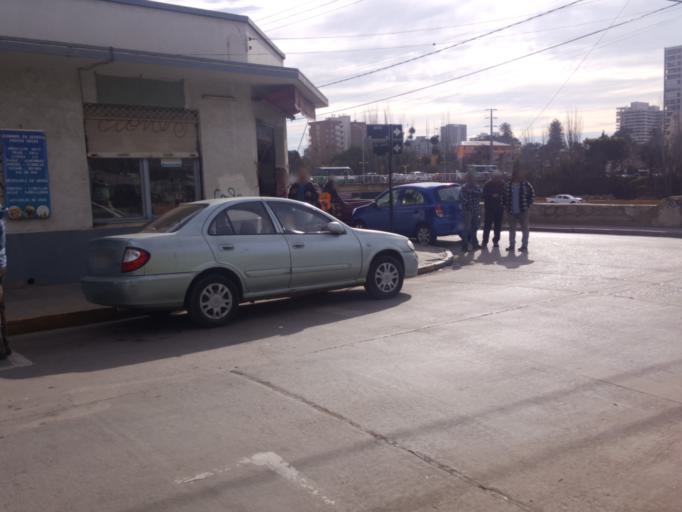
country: CL
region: Valparaiso
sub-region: Provincia de Valparaiso
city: Vina del Mar
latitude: -33.0246
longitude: -71.5448
